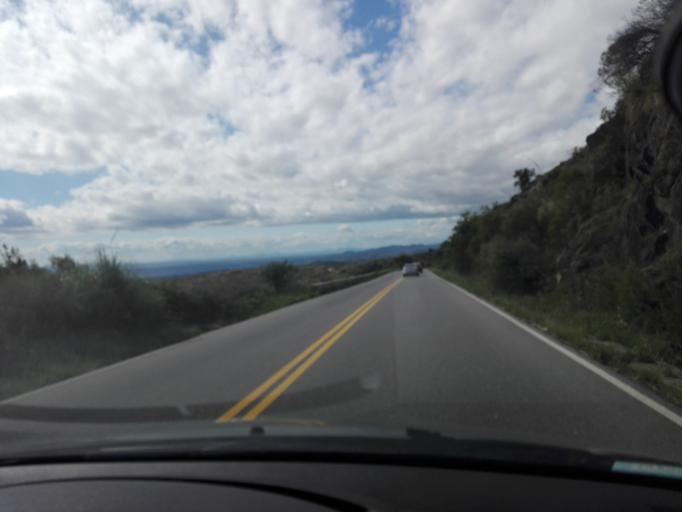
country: AR
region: Cordoba
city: Mina Clavero
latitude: -31.7645
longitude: -64.9202
